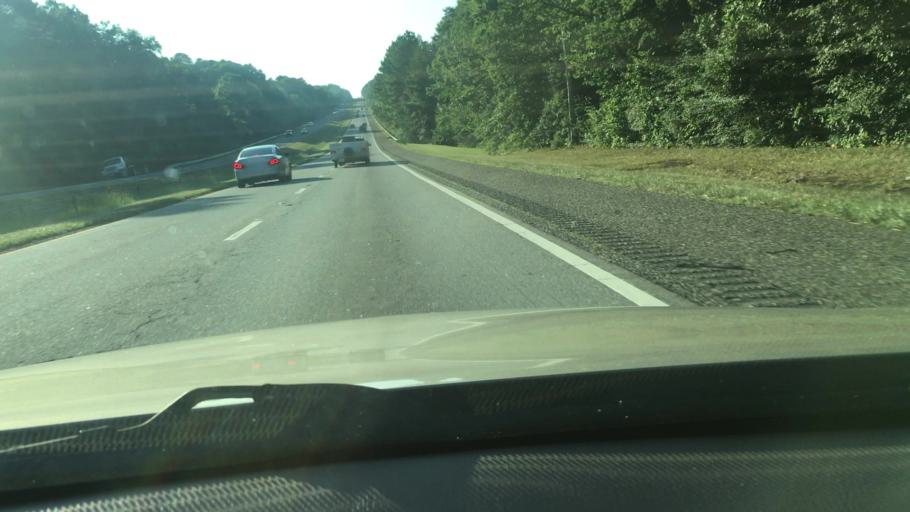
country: US
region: South Carolina
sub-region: Lexington County
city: Chapin
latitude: 34.1701
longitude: -81.3015
